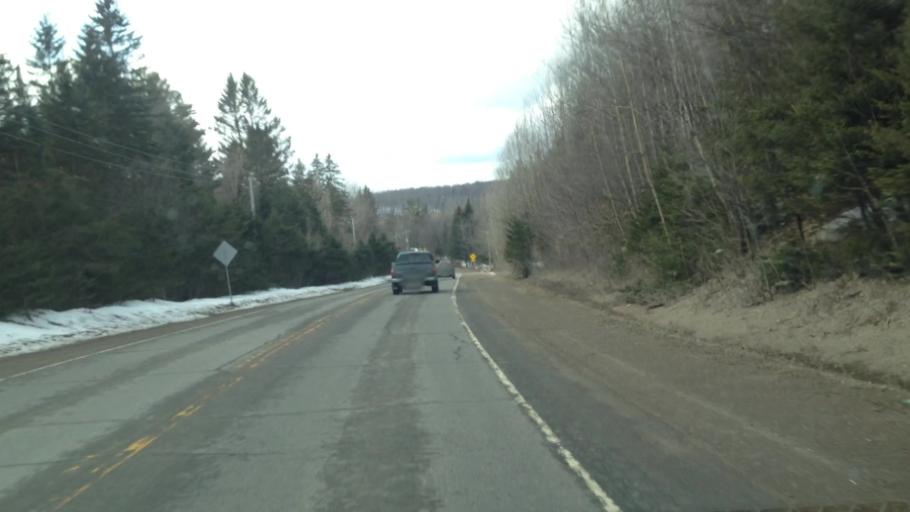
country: CA
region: Quebec
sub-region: Laurentides
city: Brownsburg-Chatham
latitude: 45.7267
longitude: -74.4701
